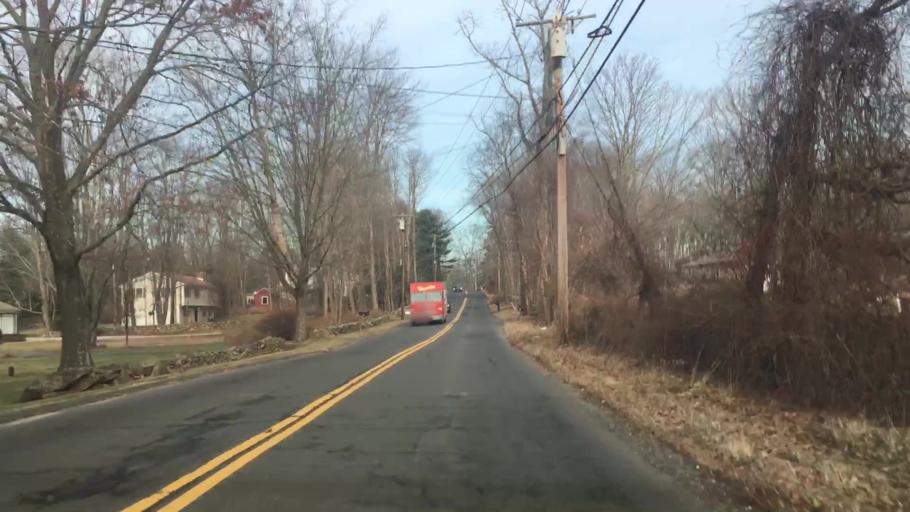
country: US
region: Connecticut
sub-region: Fairfield County
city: Newtown
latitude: 41.3943
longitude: -73.2587
